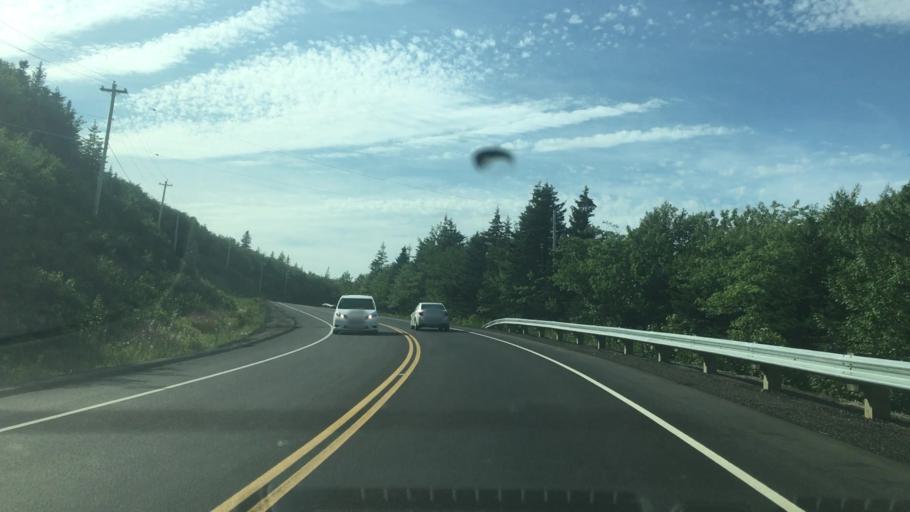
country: CA
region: Nova Scotia
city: Sydney Mines
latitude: 46.8368
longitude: -60.3805
